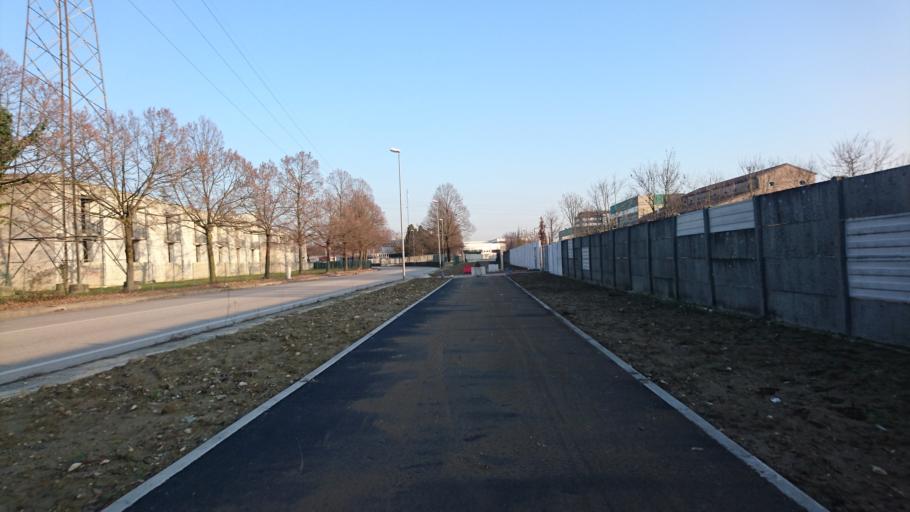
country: IT
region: Veneto
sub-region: Provincia di Padova
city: Noventa
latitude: 45.3960
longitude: 11.9418
